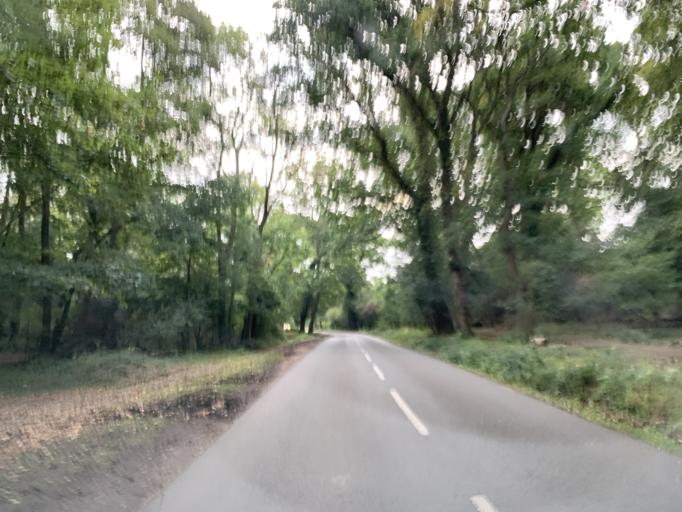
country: GB
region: England
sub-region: Hampshire
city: Brockenhurst
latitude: 50.8232
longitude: -1.5914
